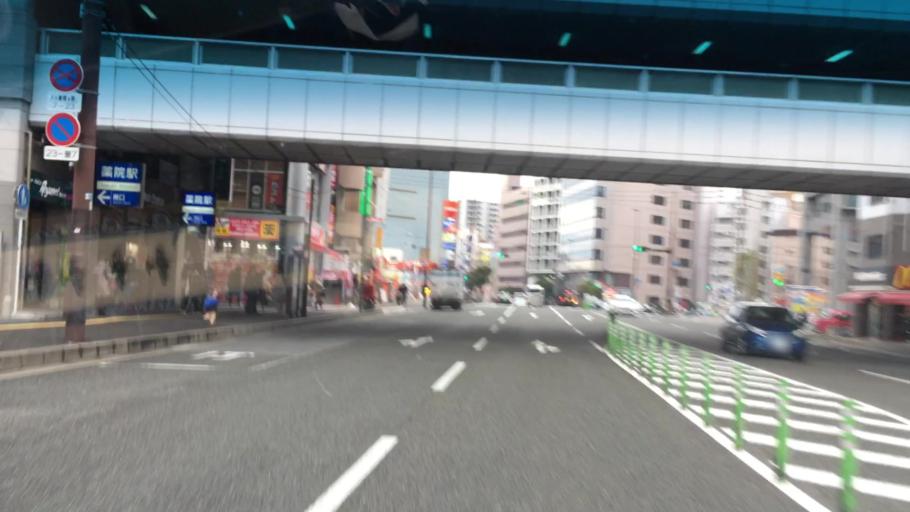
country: JP
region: Fukuoka
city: Fukuoka-shi
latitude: 33.5817
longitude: 130.4019
